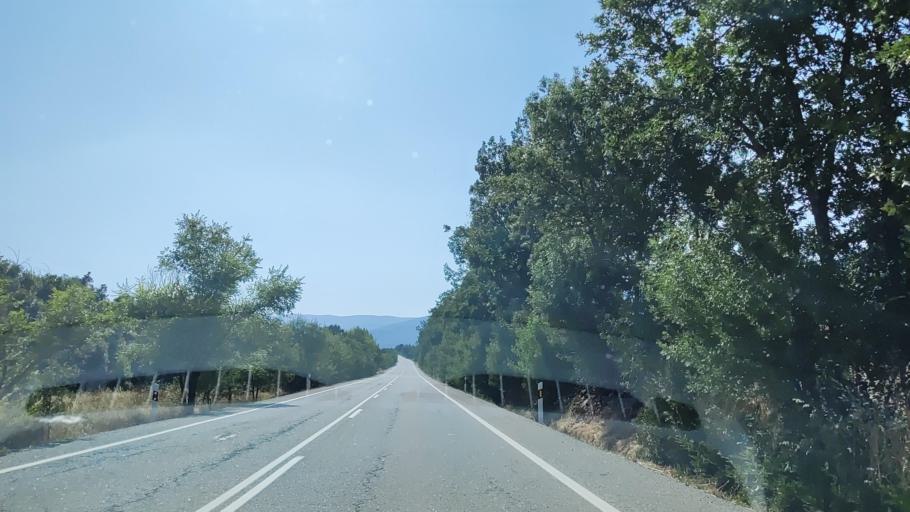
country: ES
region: Madrid
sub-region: Provincia de Madrid
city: Canencia
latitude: 40.9467
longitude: -3.7433
